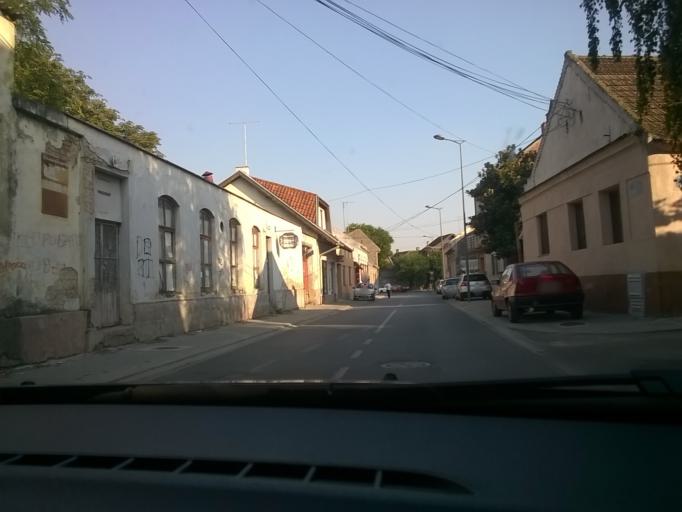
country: RS
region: Autonomna Pokrajina Vojvodina
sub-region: Juznobanatski Okrug
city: Vrsac
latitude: 45.1158
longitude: 21.2956
